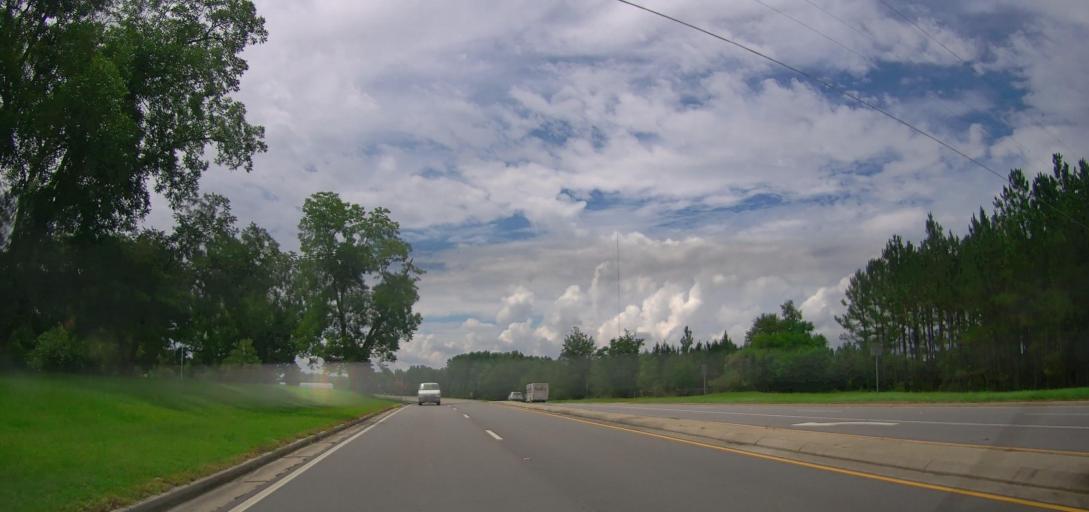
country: US
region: Georgia
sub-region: Telfair County
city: McRae
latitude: 32.0544
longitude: -82.8639
